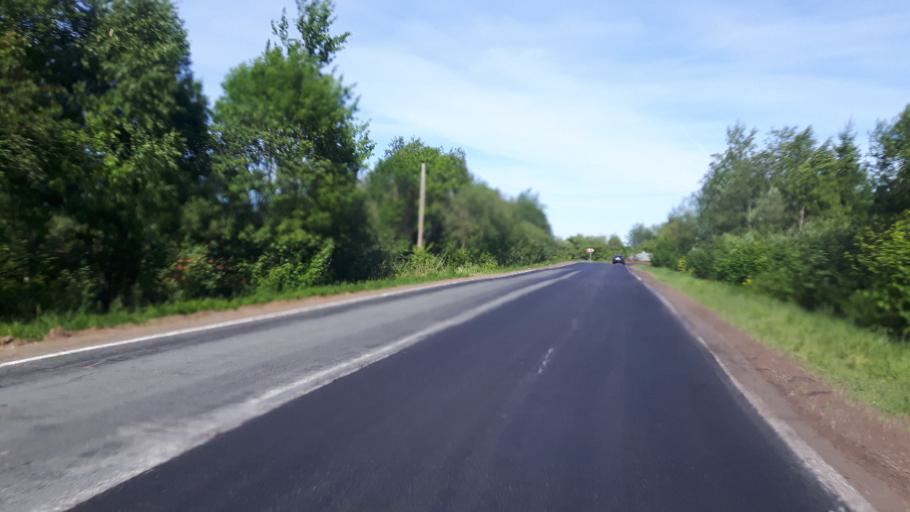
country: RU
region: Leningrad
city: Ivangorod
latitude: 59.4177
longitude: 28.3395
